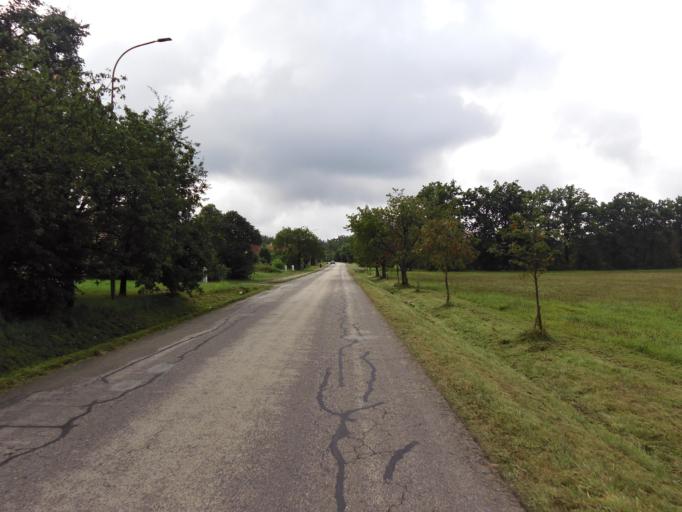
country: CZ
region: Jihocesky
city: Chlum u Trebone
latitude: 48.9655
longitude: 14.9526
